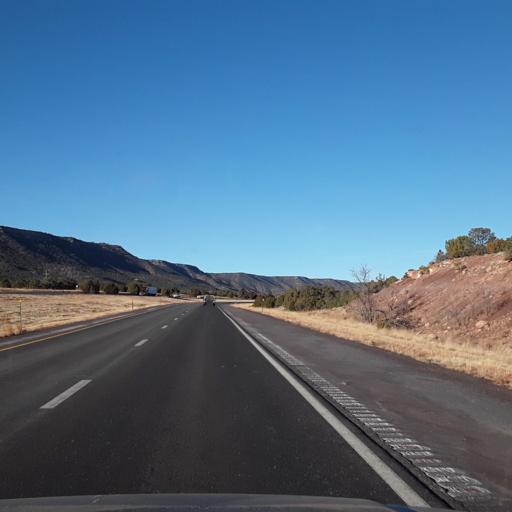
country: US
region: New Mexico
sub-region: San Miguel County
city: Pecos
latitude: 35.4155
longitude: -105.5346
